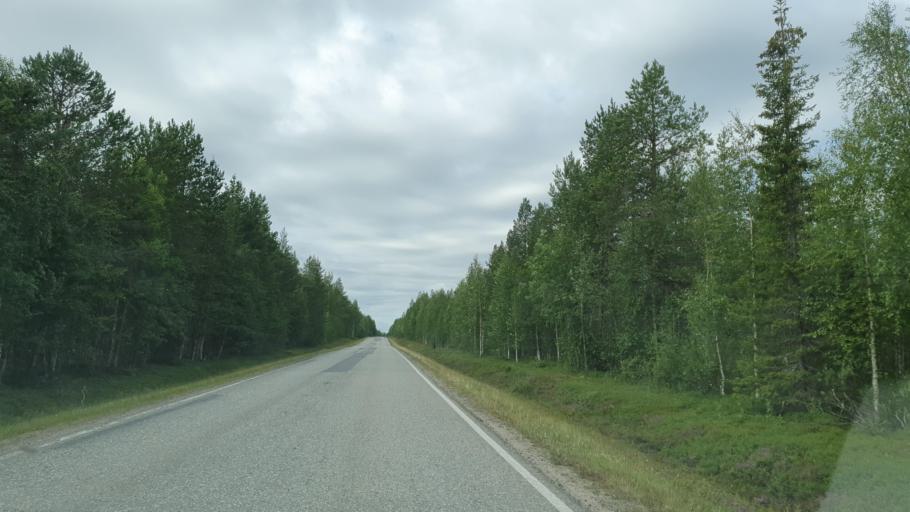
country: FI
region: Lapland
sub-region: Tunturi-Lappi
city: Kittilae
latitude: 67.6114
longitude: 25.3002
